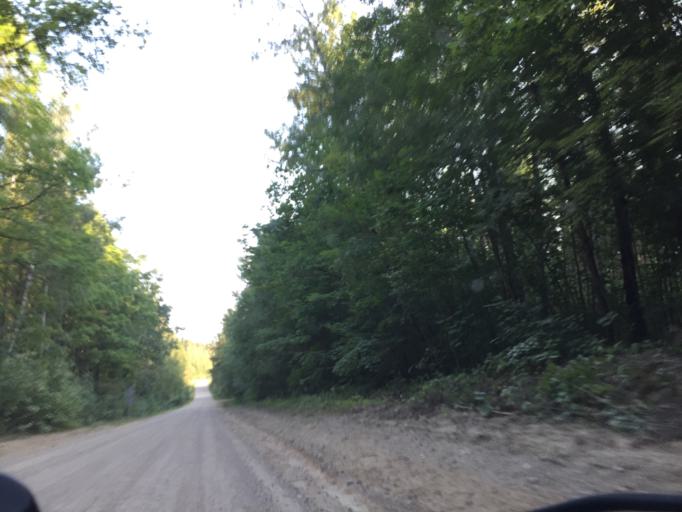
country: LV
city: Tervete
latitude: 56.4792
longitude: 23.3749
